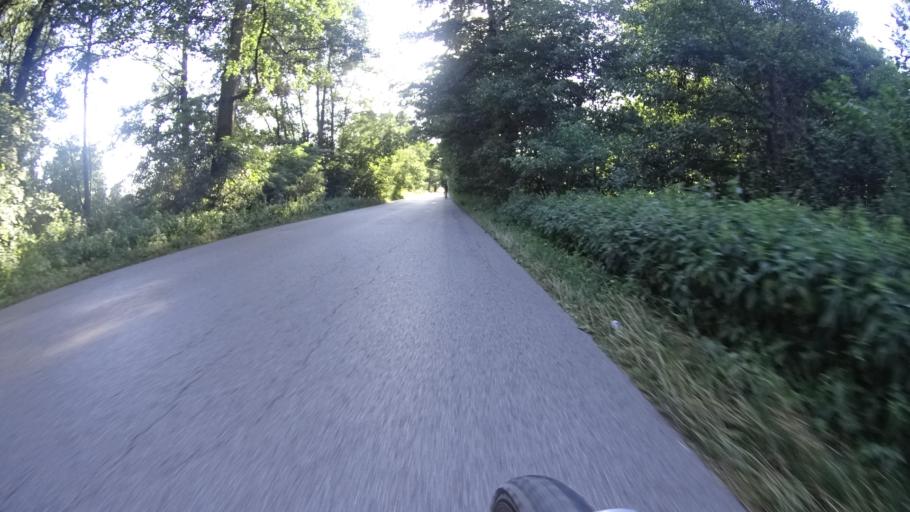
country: PL
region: Masovian Voivodeship
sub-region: Powiat bialobrzeski
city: Wysmierzyce
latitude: 51.6624
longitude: 20.8413
